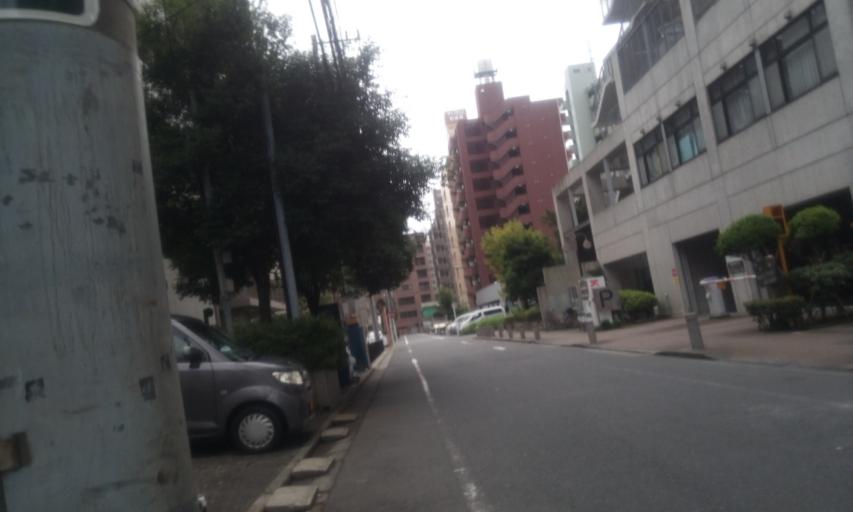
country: JP
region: Tokyo
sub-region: Machida-shi
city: Machida
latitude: 35.5781
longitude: 139.3759
